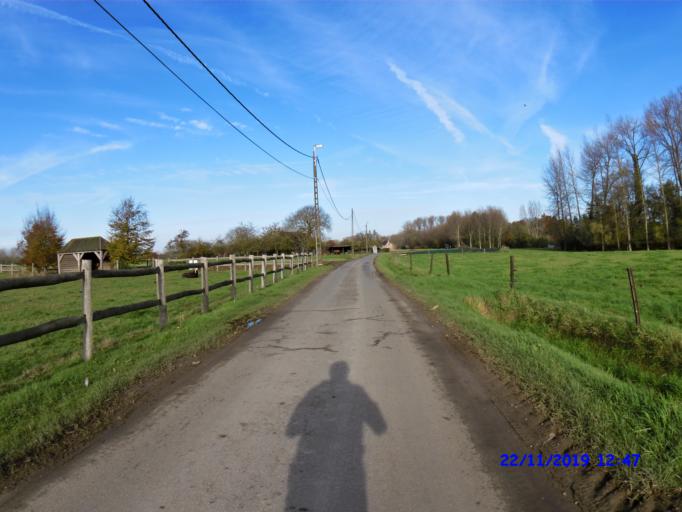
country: BE
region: Flanders
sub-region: Provincie Vlaams-Brabant
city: Merchtem
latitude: 50.9682
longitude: 4.2700
